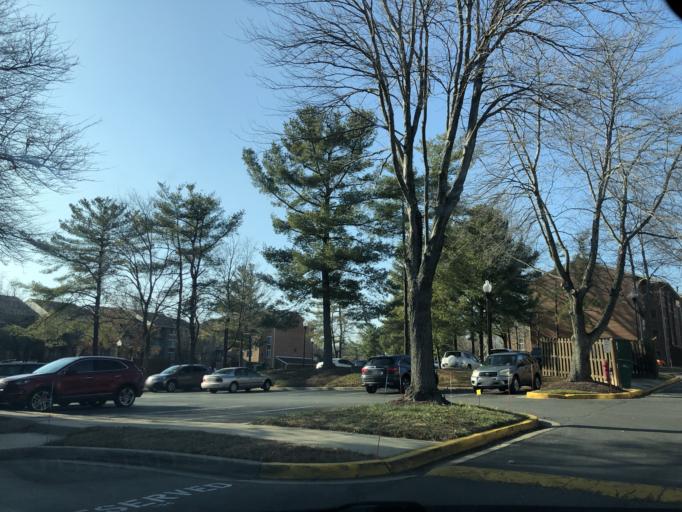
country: US
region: Maryland
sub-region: Montgomery County
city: Burtonsville
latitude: 39.1047
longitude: -76.9299
